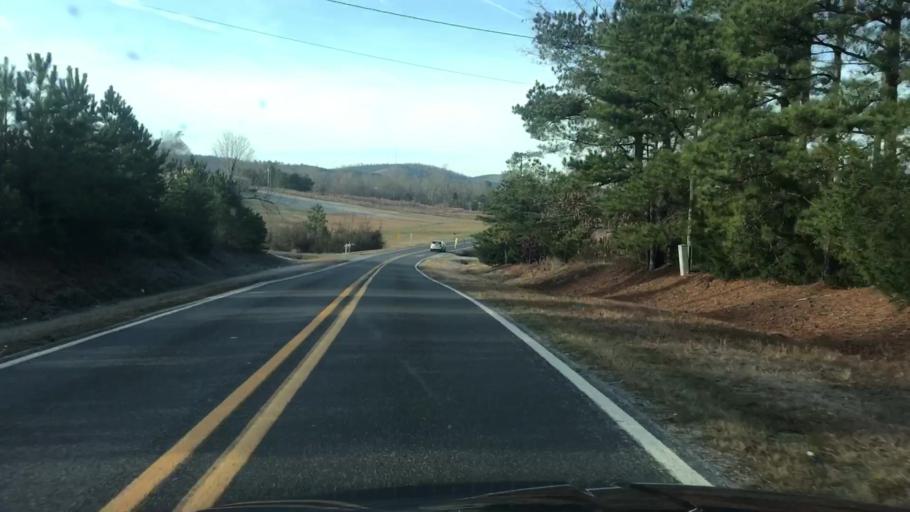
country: US
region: Arkansas
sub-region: Garland County
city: Rockwell
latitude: 34.4732
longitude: -93.2405
